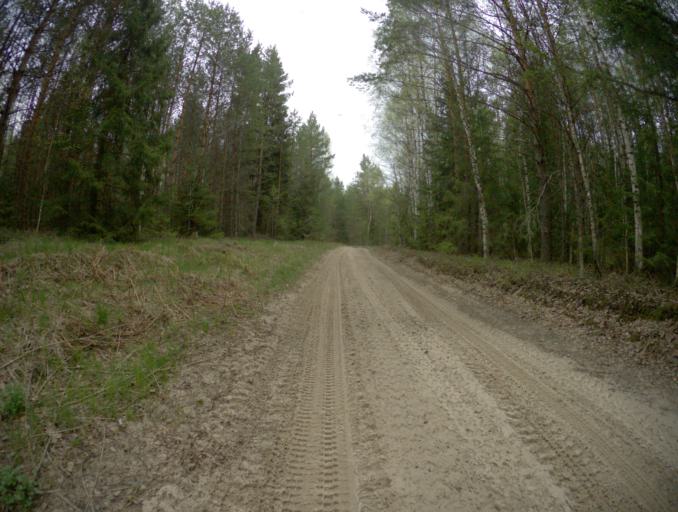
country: RU
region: Vladimir
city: Golovino
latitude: 55.8896
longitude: 40.4084
